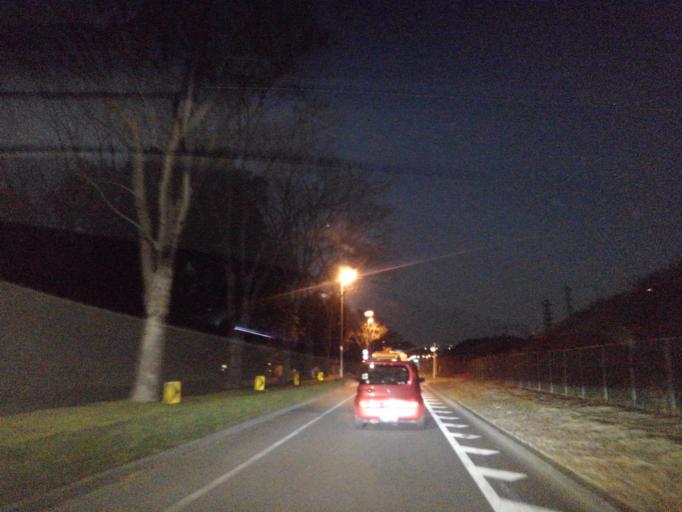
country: JP
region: Tokyo
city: Hino
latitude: 35.6236
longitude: 139.4606
